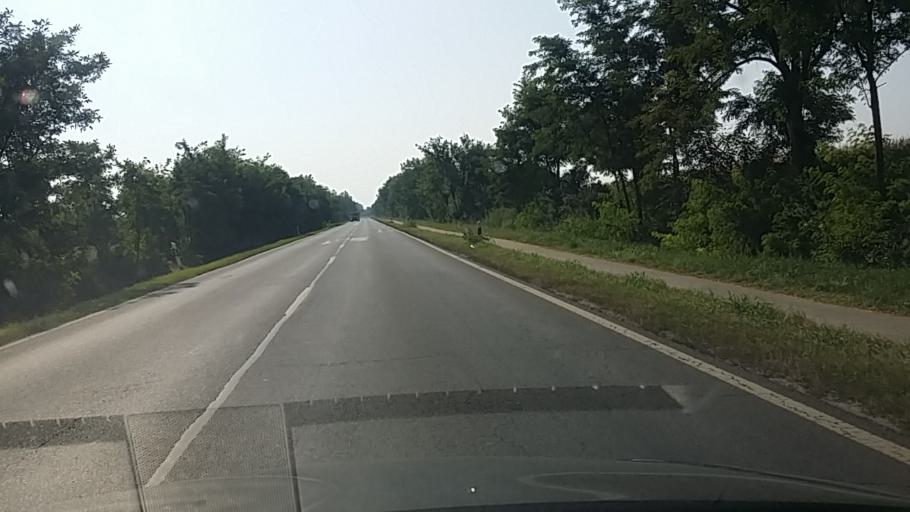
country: HU
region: Bekes
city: Csorvas
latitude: 46.7226
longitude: 20.9262
